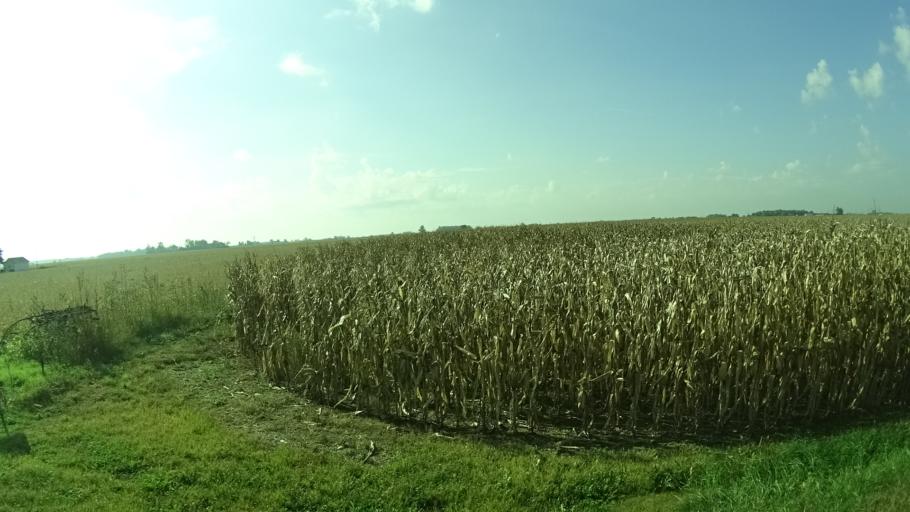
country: US
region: Indiana
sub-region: Madison County
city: Lapel
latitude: 40.0458
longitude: -85.8149
